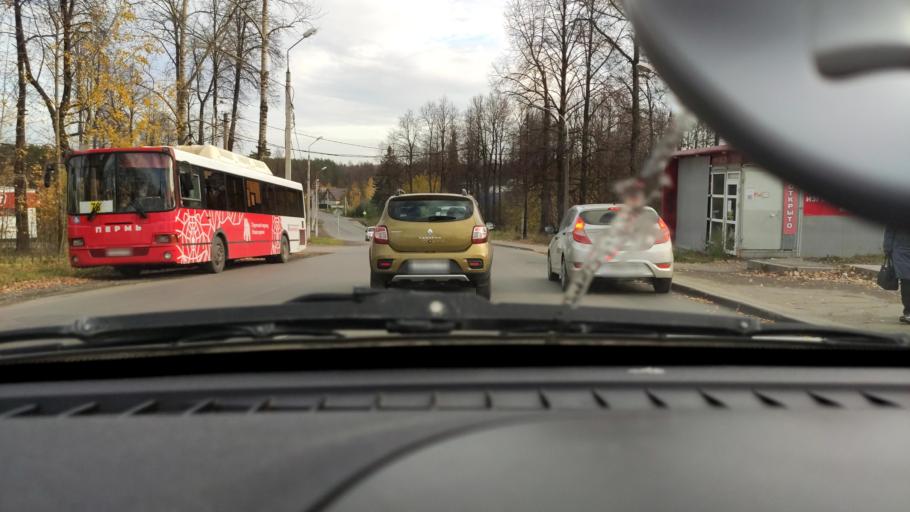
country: RU
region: Perm
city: Perm
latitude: 58.0888
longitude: 56.4017
